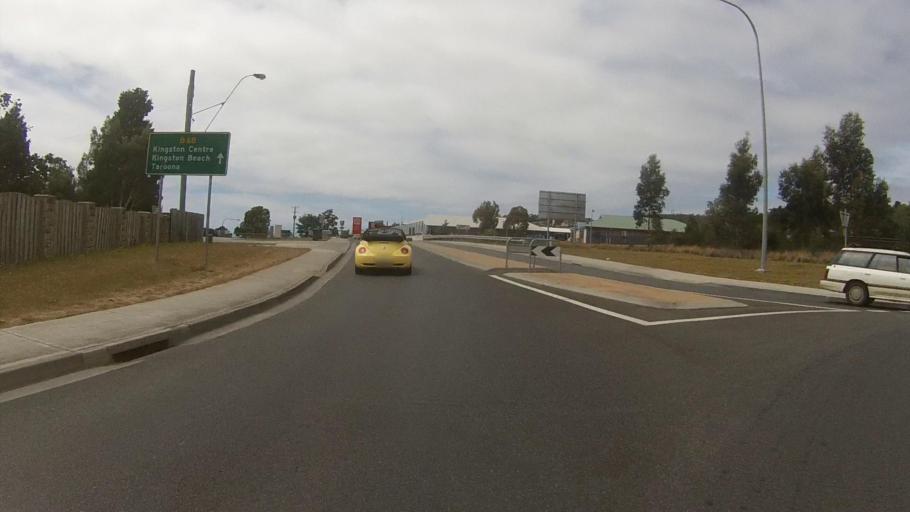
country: AU
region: Tasmania
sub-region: Kingborough
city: Kingston
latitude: -42.9748
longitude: 147.3006
